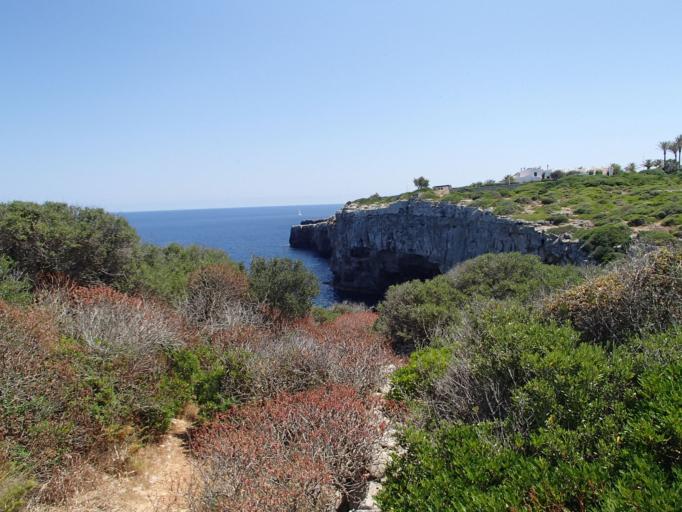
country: ES
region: Balearic Islands
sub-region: Illes Balears
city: Es Castell
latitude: 39.8413
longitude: 4.2995
